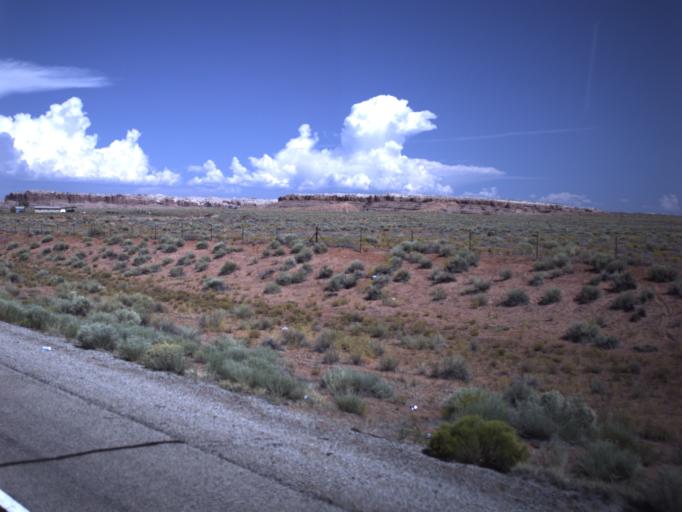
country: US
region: Utah
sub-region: San Juan County
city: Blanding
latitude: 37.1649
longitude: -109.5762
